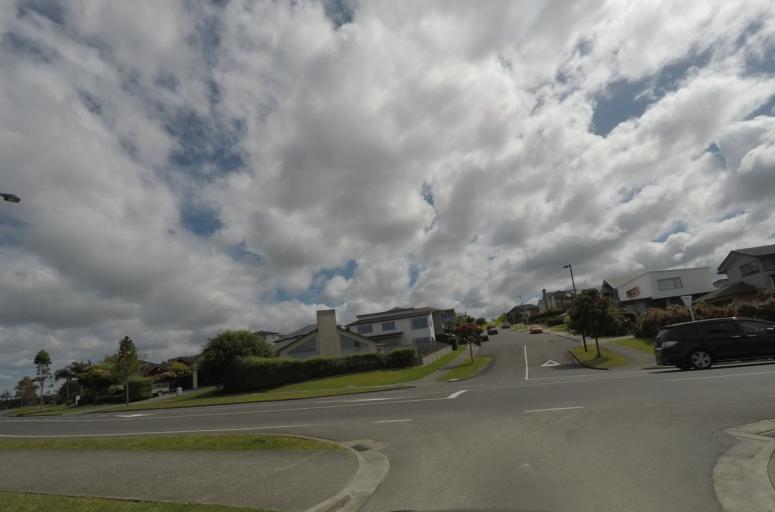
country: NZ
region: Auckland
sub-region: Auckland
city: Rothesay Bay
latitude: -36.5988
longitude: 174.6785
